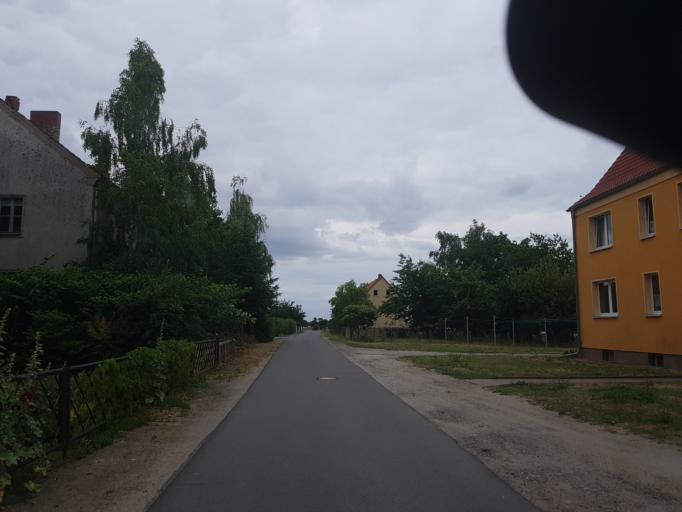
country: DE
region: Saxony-Anhalt
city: Kropstadt
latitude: 52.0023
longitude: 12.7816
